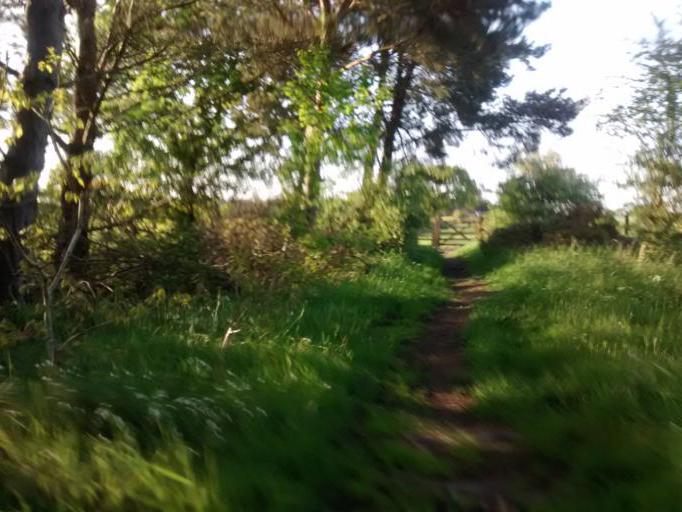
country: GB
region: England
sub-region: County Durham
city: West Cornforth
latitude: 54.7346
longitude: -1.5470
